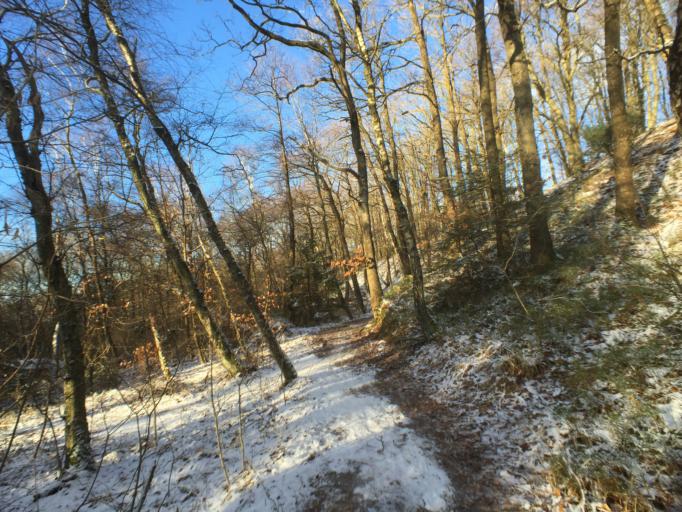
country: DK
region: Central Jutland
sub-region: Silkeborg Kommune
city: Svejbaek
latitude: 56.2202
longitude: 9.6947
